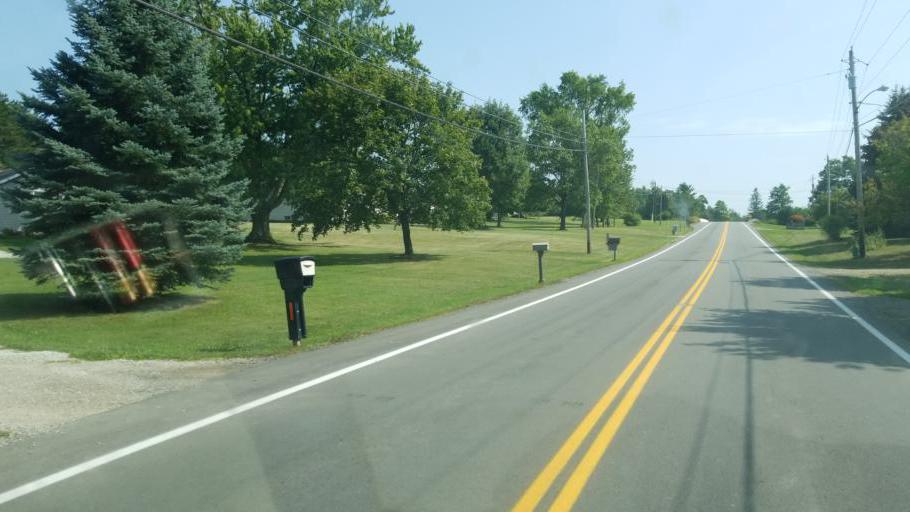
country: US
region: Ohio
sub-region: Richland County
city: Ontario
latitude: 40.7834
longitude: -82.6539
